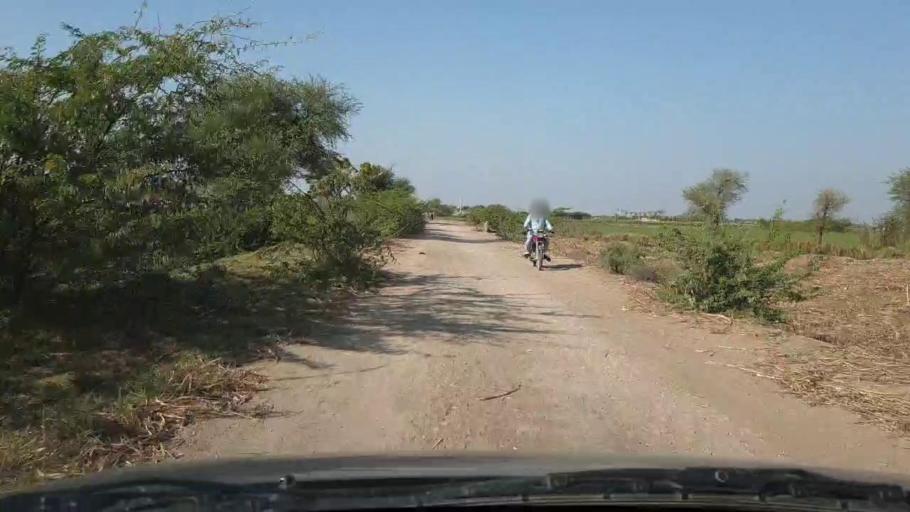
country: PK
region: Sindh
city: Samaro
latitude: 25.1756
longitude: 69.2835
